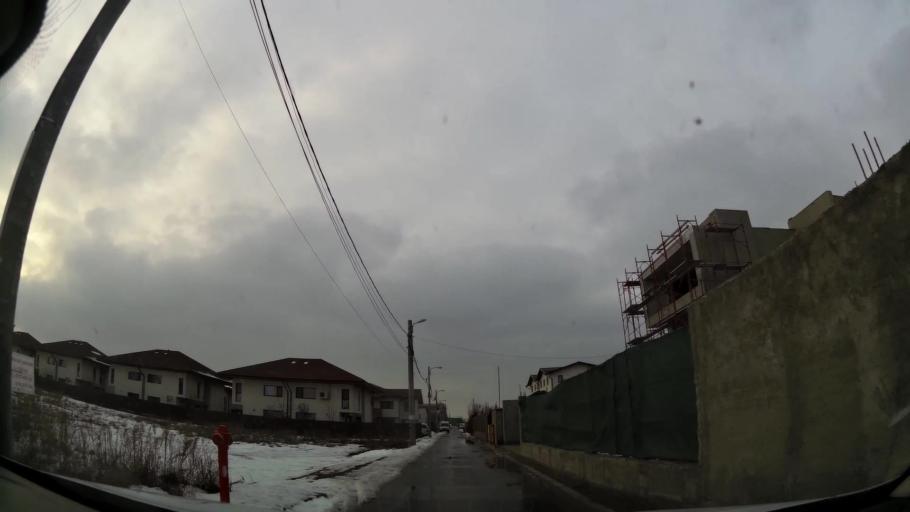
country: RO
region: Ilfov
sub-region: Voluntari City
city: Voluntari
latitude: 44.4972
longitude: 26.1651
